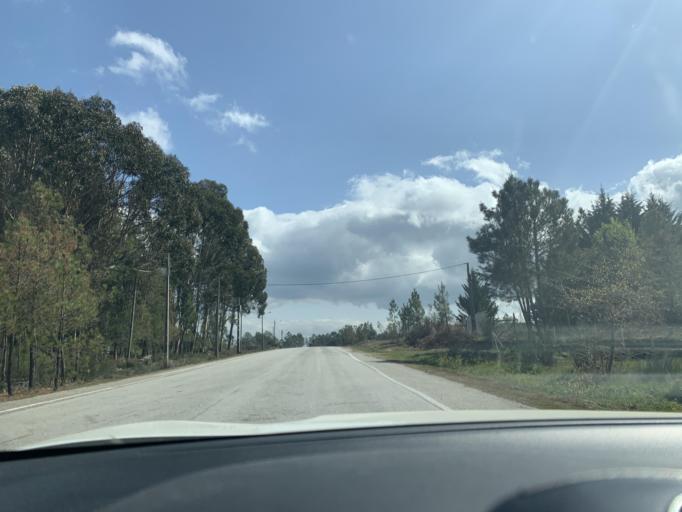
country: PT
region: Guarda
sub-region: Fornos de Algodres
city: Fornos de Algodres
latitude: 40.6166
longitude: -7.6128
